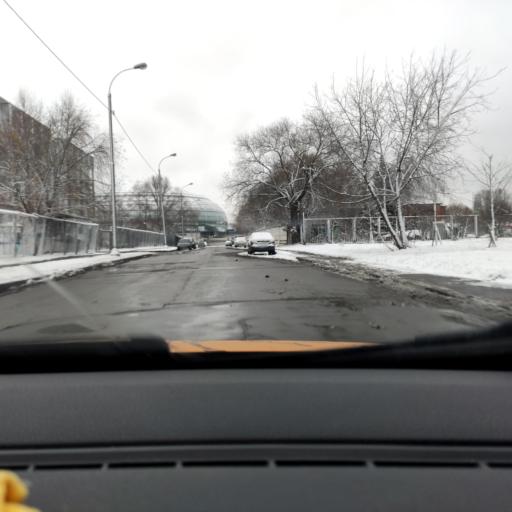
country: RU
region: Moskovskaya
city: Fili
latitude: 55.7549
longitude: 37.4430
